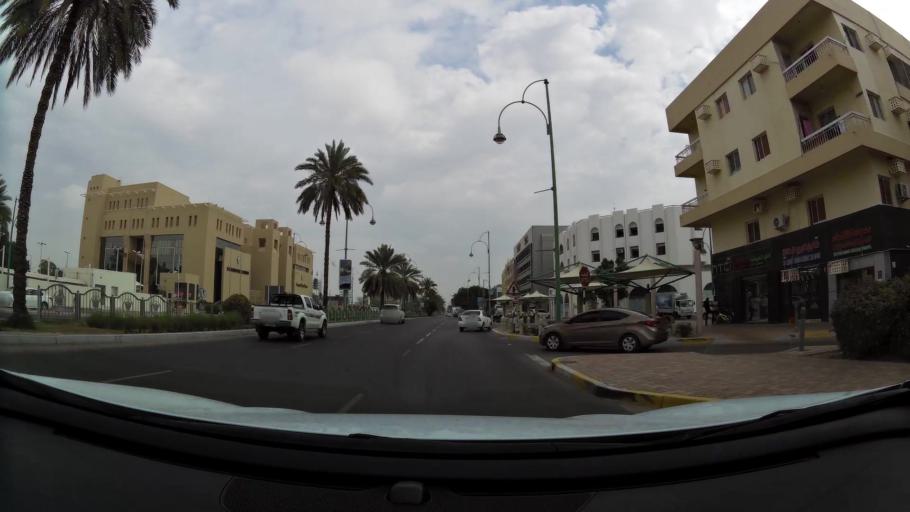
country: AE
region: Abu Dhabi
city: Al Ain
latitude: 24.2200
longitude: 55.7762
